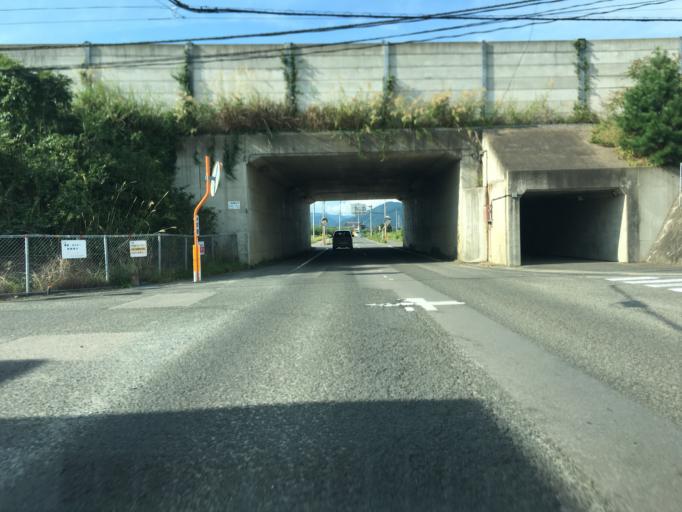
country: JP
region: Fukushima
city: Fukushima-shi
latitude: 37.8032
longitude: 140.4588
